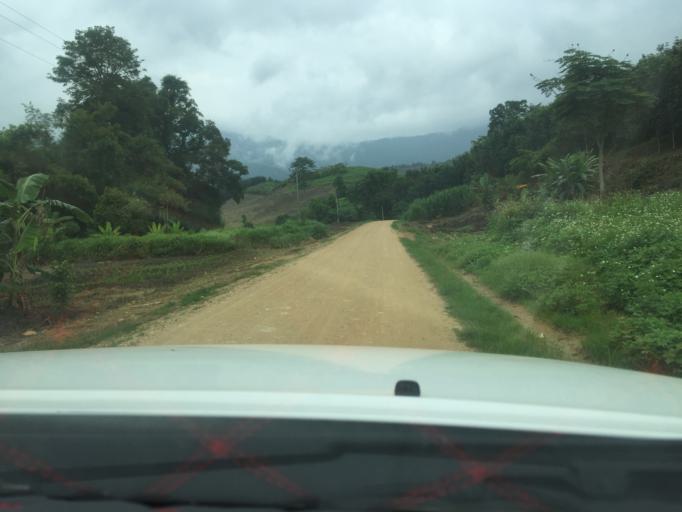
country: TH
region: Phayao
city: Phu Sang
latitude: 19.7428
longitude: 100.4562
